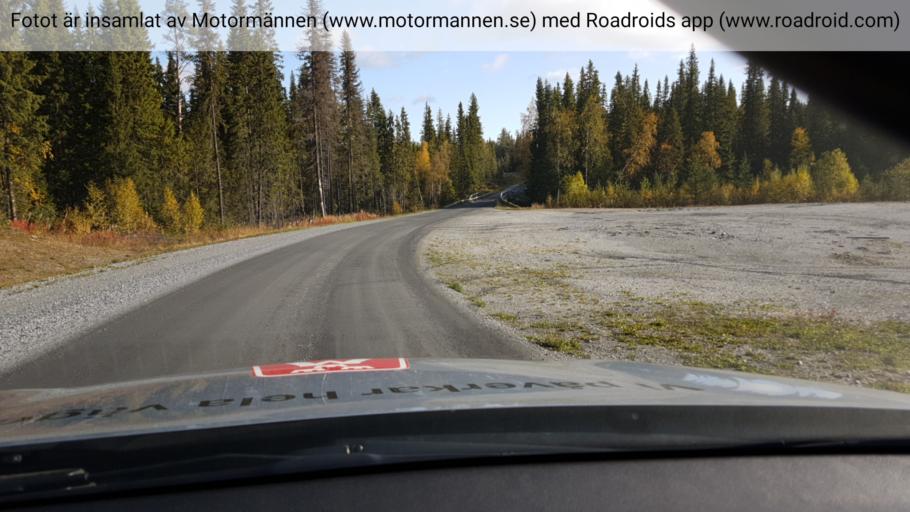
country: SE
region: Vaesterbotten
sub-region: Vilhelmina Kommun
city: Sjoberg
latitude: 64.8000
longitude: 15.9987
